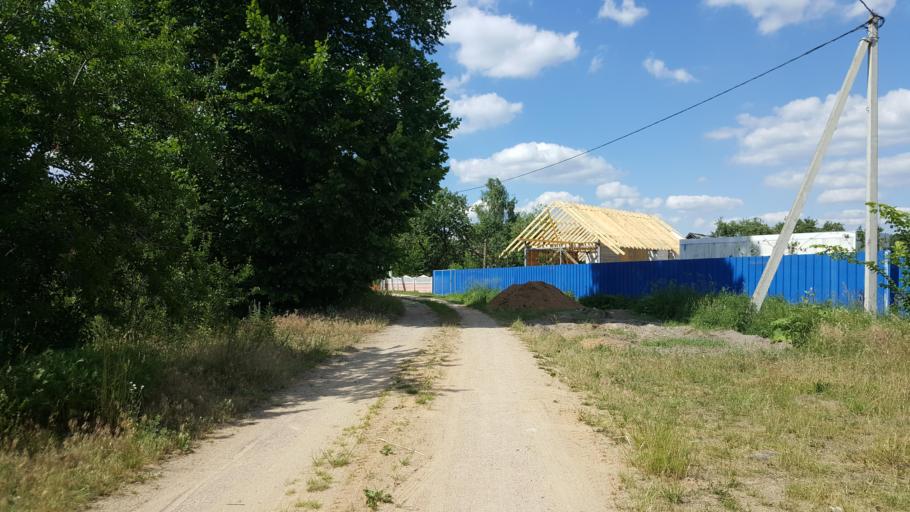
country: BY
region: Brest
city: Kamyanyuki
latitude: 52.5043
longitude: 23.6919
